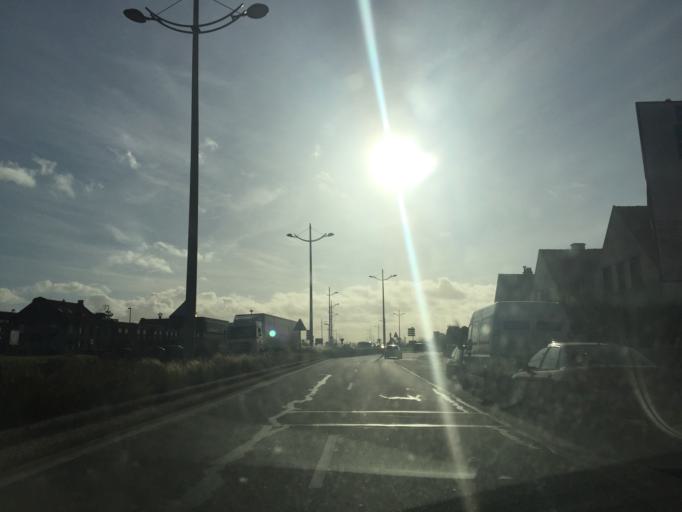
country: FR
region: Nord-Pas-de-Calais
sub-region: Departement du Pas-de-Calais
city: Calais
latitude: 50.9473
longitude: 1.8381
